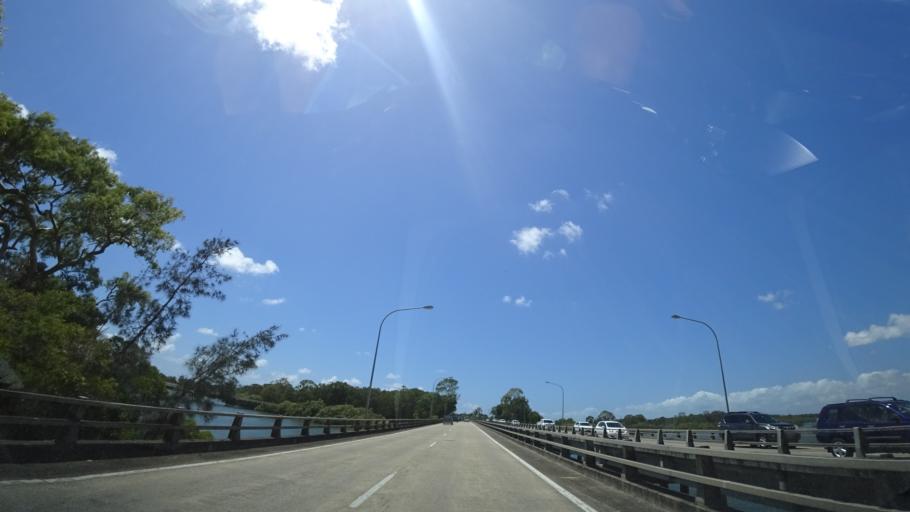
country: AU
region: Queensland
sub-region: Sunshine Coast
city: Mooloolaba
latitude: -26.6961
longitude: 153.1142
